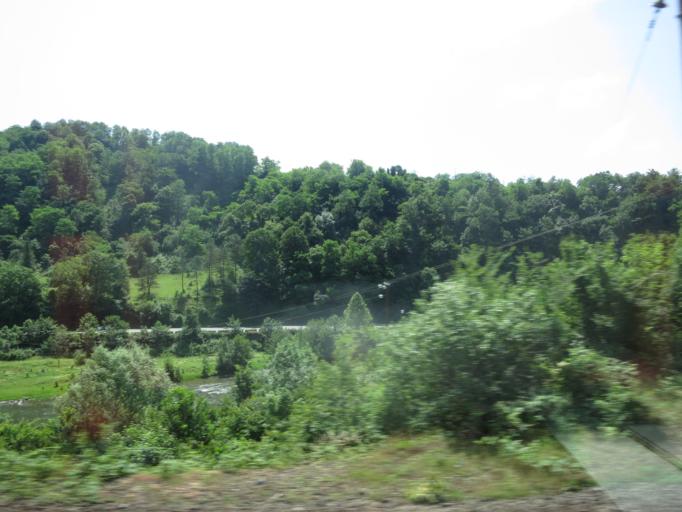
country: GE
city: Shorapani
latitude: 42.0942
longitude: 43.1020
